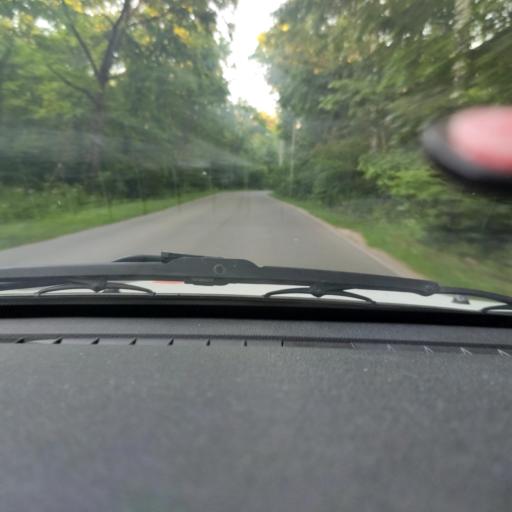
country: RU
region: Voronezj
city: Ramon'
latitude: 51.8953
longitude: 39.2829
